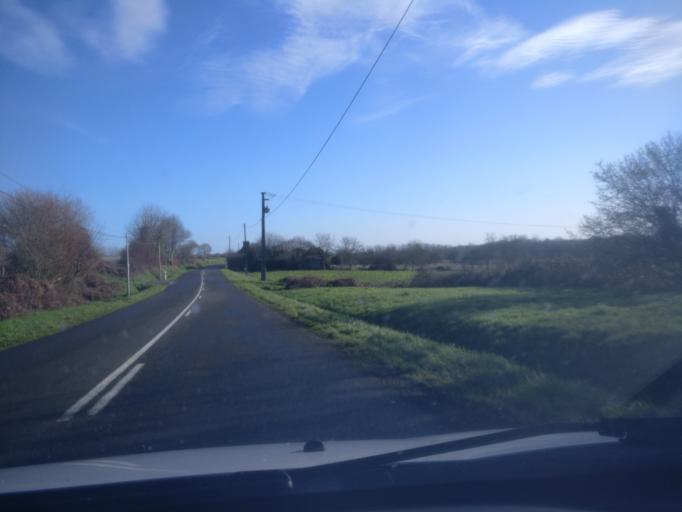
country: FR
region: Brittany
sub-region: Departement d'Ille-et-Vilaine
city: Pleine-Fougeres
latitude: 48.5431
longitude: -1.6136
